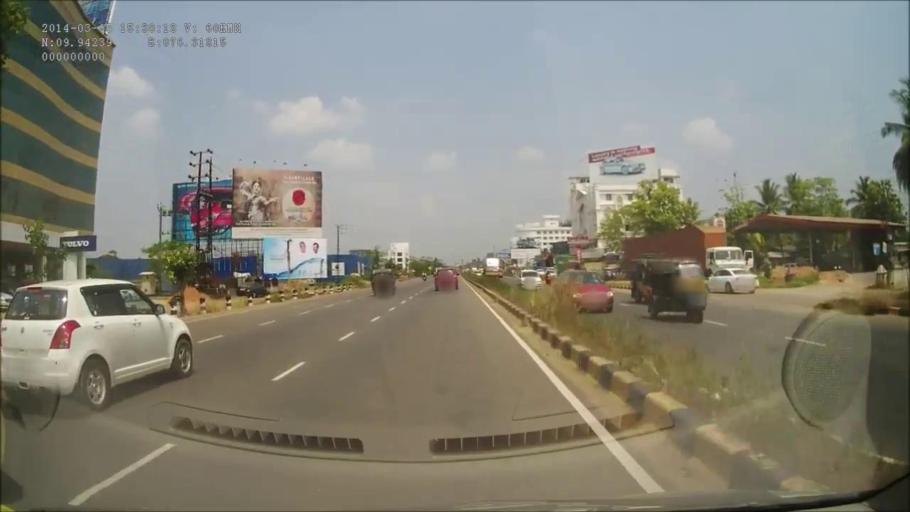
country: IN
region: Kerala
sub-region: Ernakulam
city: Cochin
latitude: 9.9437
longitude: 76.3181
